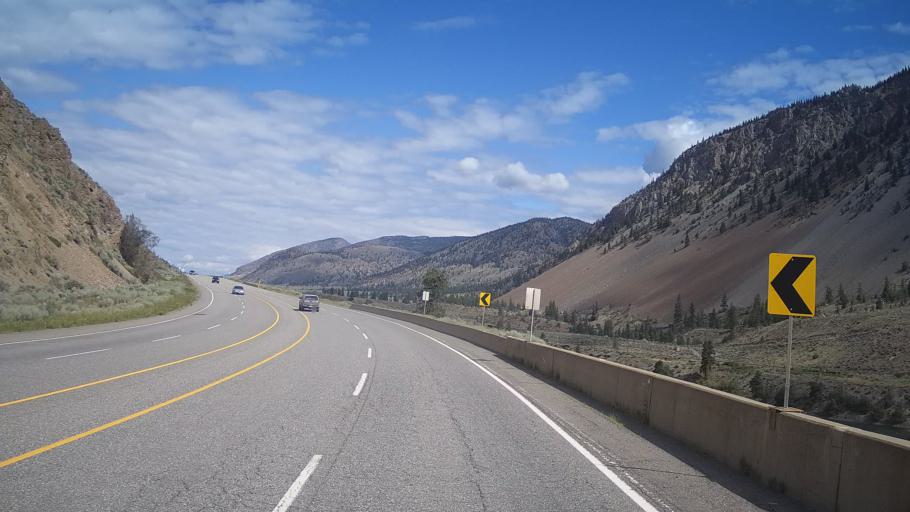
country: CA
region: British Columbia
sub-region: Thompson-Nicola Regional District
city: Ashcroft
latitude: 50.5122
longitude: -121.2811
